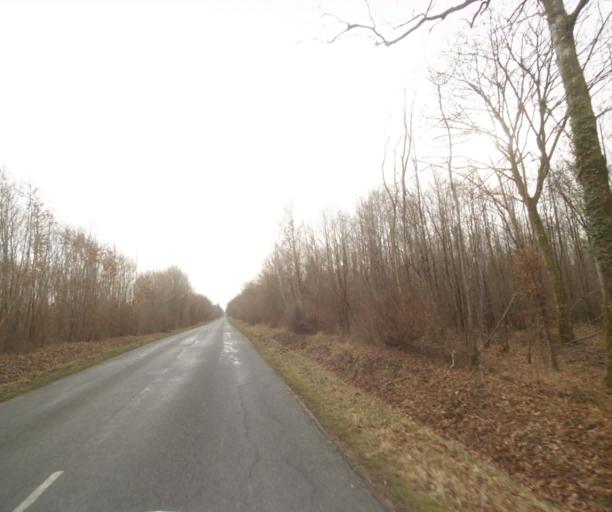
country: FR
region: Champagne-Ardenne
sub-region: Departement de la Marne
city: Pargny-sur-Saulx
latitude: 48.7251
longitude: 4.8712
